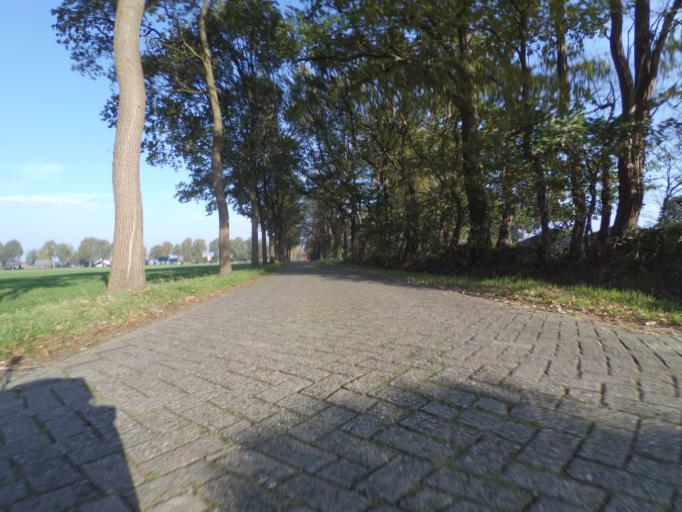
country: NL
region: Gelderland
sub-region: Gemeente Putten
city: Putten
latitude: 52.2238
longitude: 5.5832
